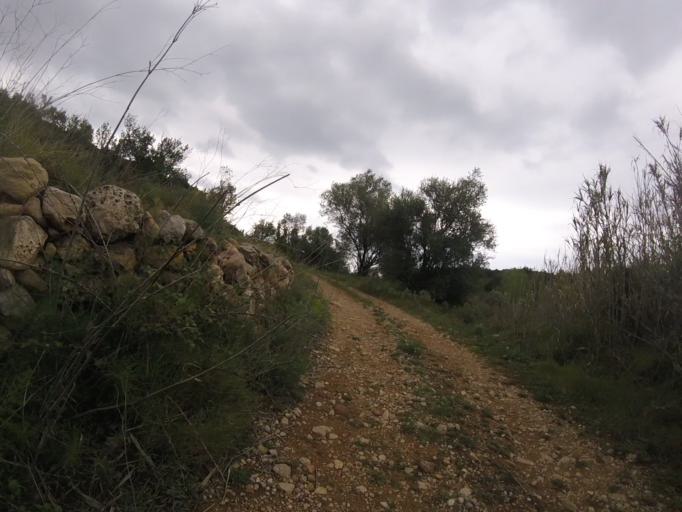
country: ES
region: Valencia
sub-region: Provincia de Castello
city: Cuevas de Vinroma
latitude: 40.2927
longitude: 0.0860
